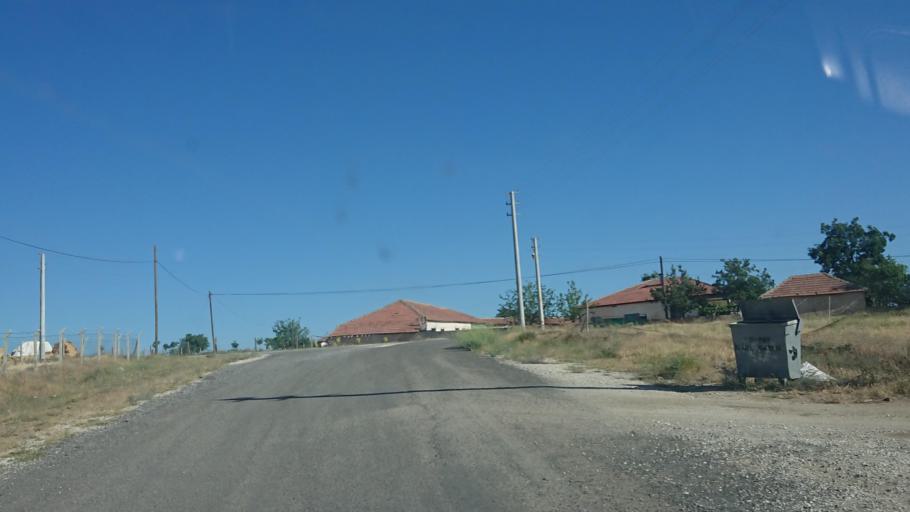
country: TR
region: Aksaray
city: Agacoren
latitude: 38.8779
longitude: 33.9515
